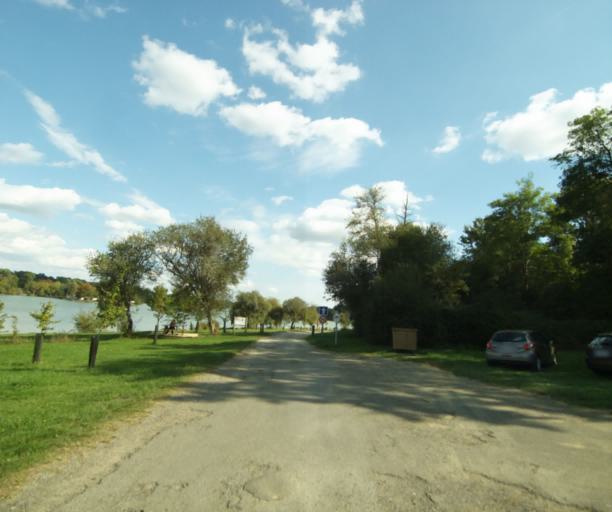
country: FR
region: Midi-Pyrenees
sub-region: Departement du Gers
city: Cazaubon
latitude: 43.9381
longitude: -0.0525
